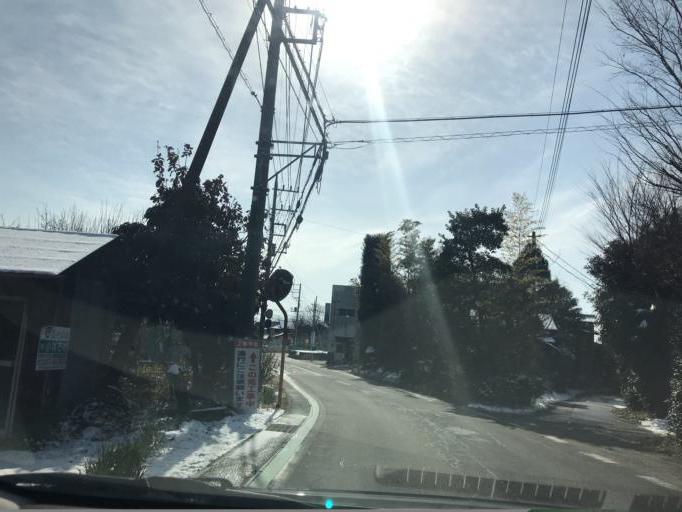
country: JP
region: Ibaraki
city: Moriya
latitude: 35.9477
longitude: 139.9632
